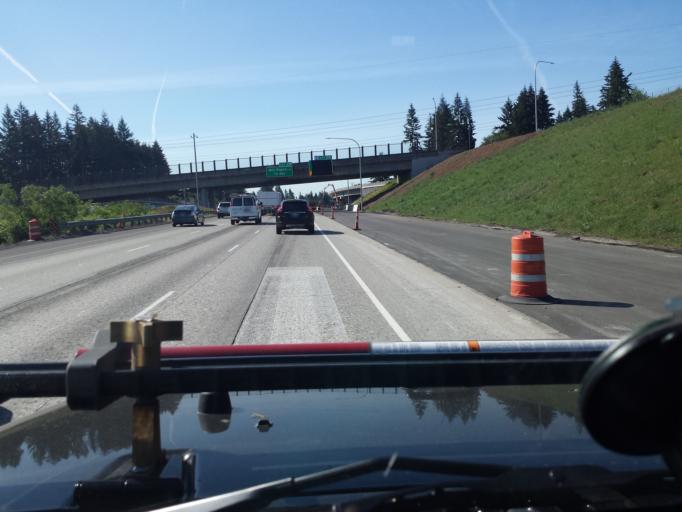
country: US
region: Washington
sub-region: Clark County
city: Orchards
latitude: 45.6367
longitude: -122.5615
